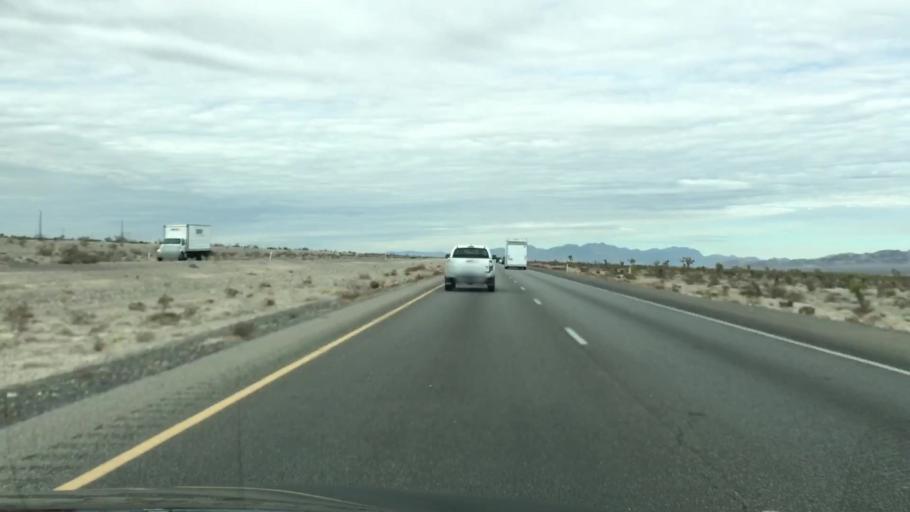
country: US
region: Nevada
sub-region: Clark County
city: Summerlin South
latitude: 36.4474
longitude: -115.4359
